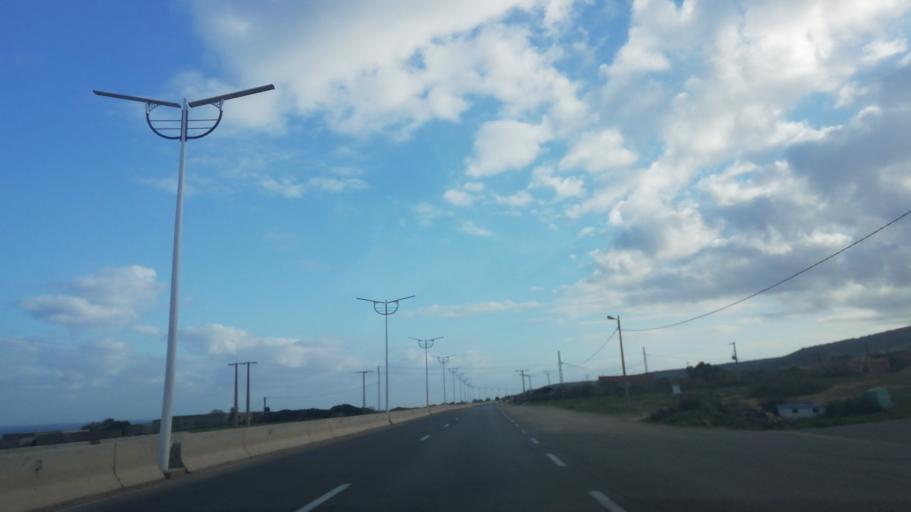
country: DZ
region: Mostaganem
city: Mostaganem
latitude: 36.0682
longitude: 0.1724
